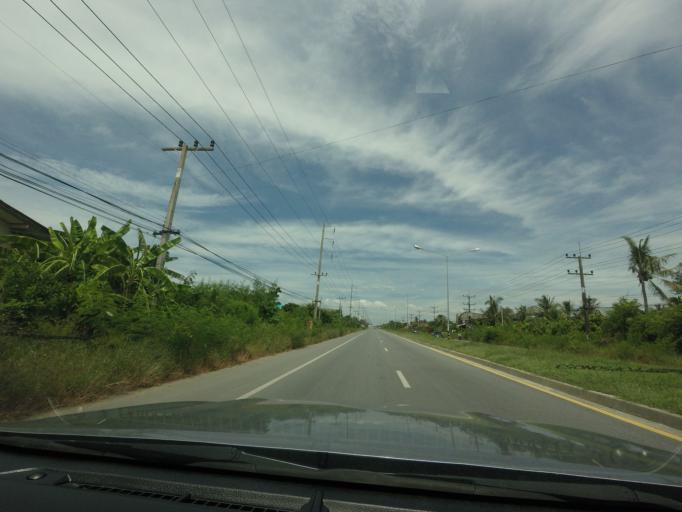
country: TH
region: Songkhla
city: Ranot
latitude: 7.7479
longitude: 100.3624
